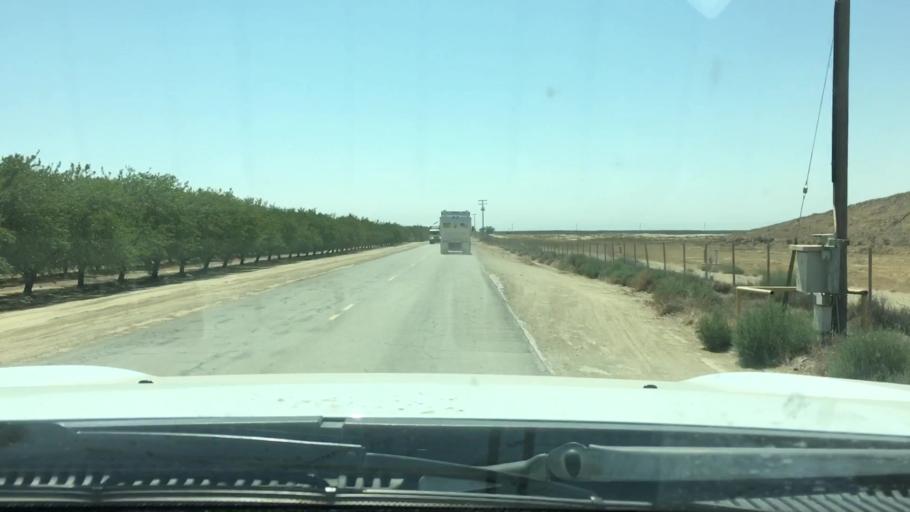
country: US
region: California
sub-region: Kern County
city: Wasco
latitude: 35.5135
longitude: -119.4033
